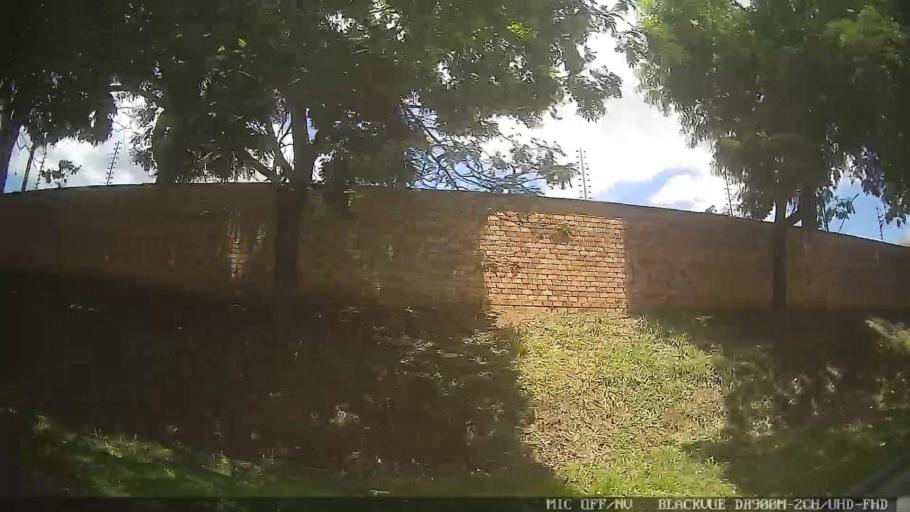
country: BR
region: Sao Paulo
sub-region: Jacarei
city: Jacarei
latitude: -23.3018
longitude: -45.9477
